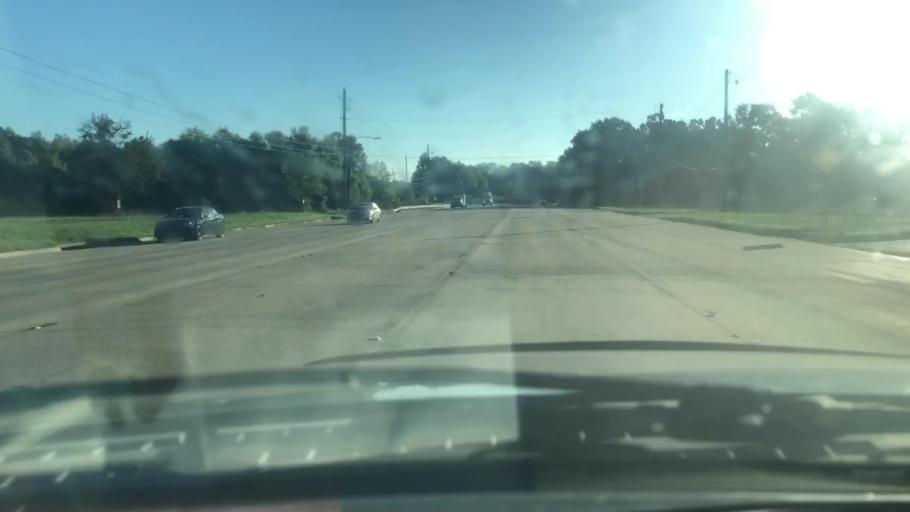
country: US
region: Texas
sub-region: Bowie County
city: Texarkana
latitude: 33.4216
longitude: -94.0749
